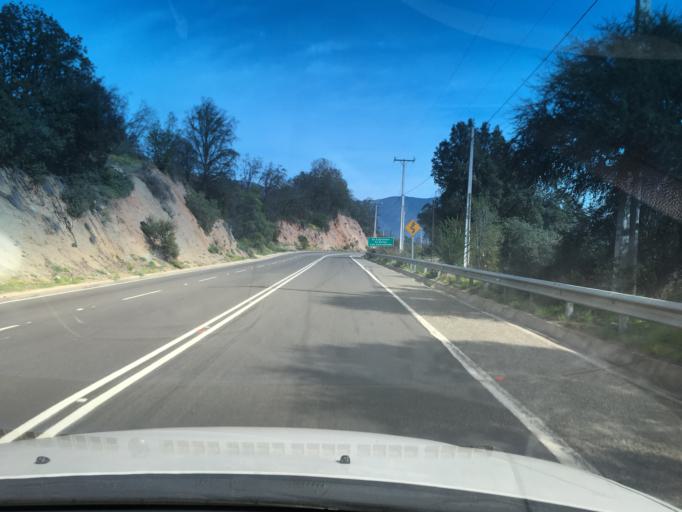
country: CL
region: Valparaiso
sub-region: Provincia de San Felipe
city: Llaillay
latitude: -33.0624
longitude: -71.0215
